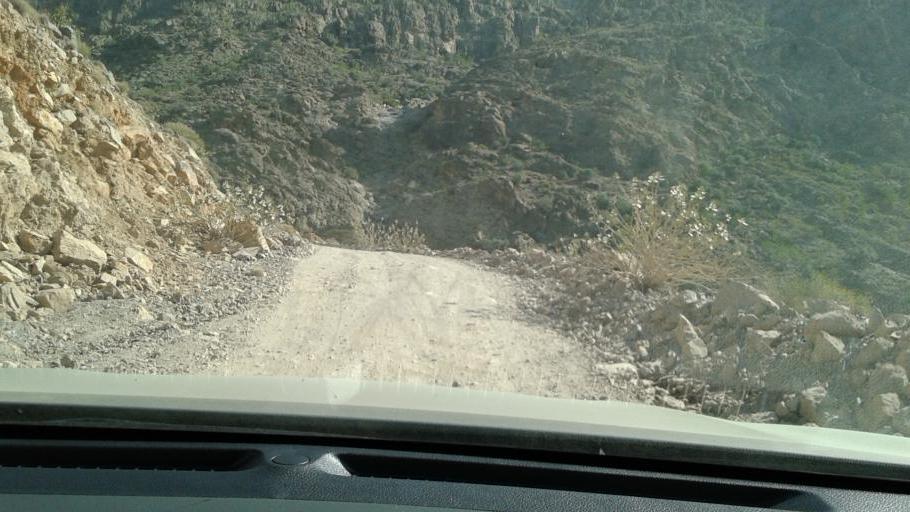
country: OM
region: Al Batinah
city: Bayt al `Awabi
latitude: 23.1783
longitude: 57.4092
